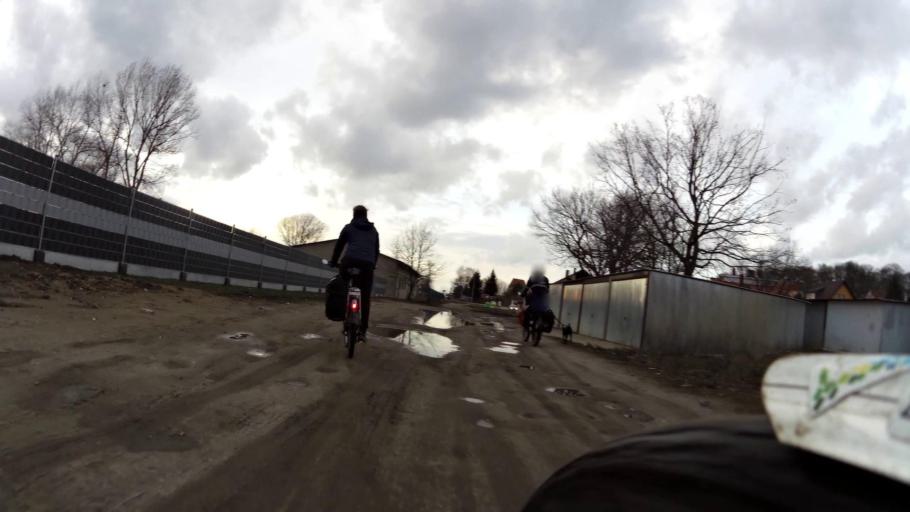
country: PL
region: West Pomeranian Voivodeship
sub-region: Powiat kamienski
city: Kamien Pomorski
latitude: 53.9666
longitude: 14.7660
